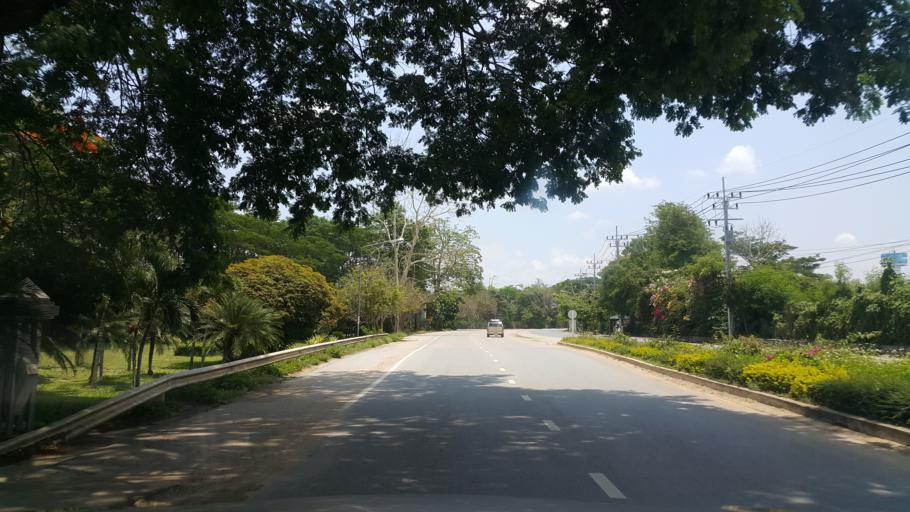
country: TH
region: Chiang Rai
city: Chiang Rai
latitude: 19.9214
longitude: 99.8195
